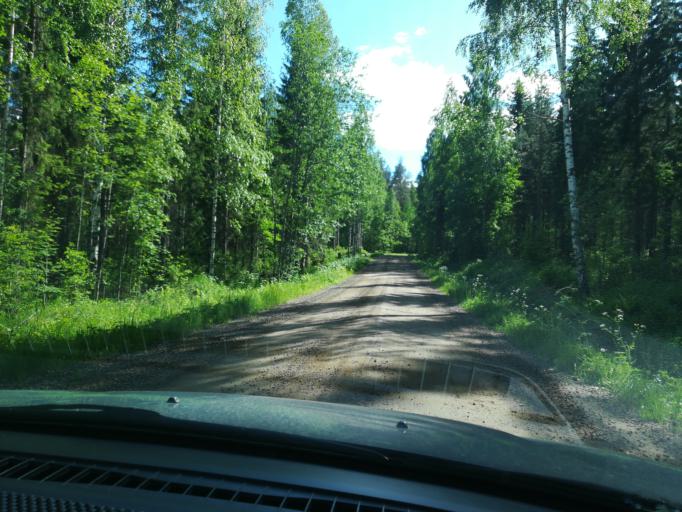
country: FI
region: Southern Savonia
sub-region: Mikkeli
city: Puumala
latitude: 61.6636
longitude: 28.1430
